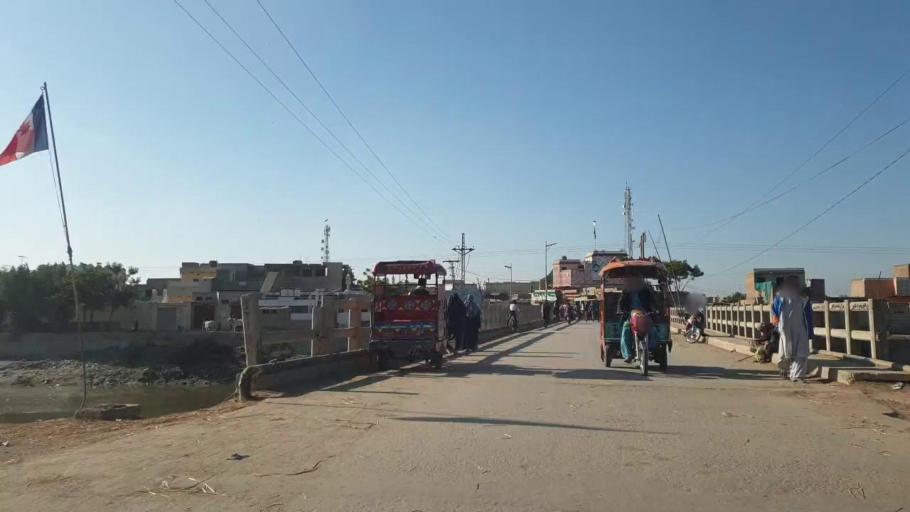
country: PK
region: Sindh
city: New Badah
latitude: 27.3293
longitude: 68.0220
